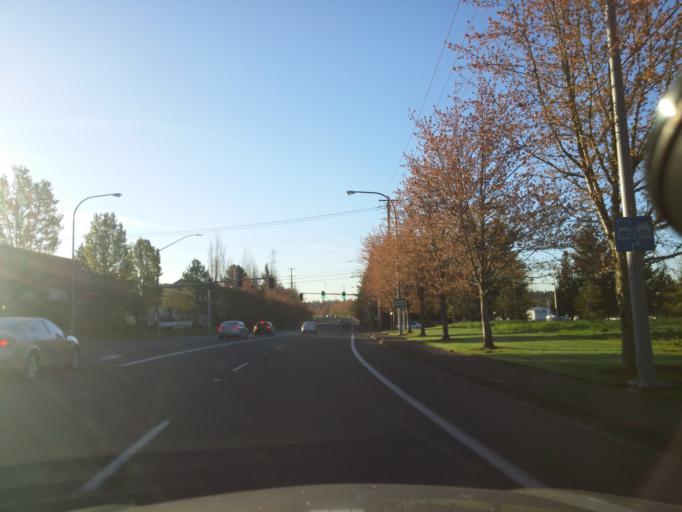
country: US
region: Oregon
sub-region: Washington County
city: Aloha
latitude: 45.5120
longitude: -122.8498
